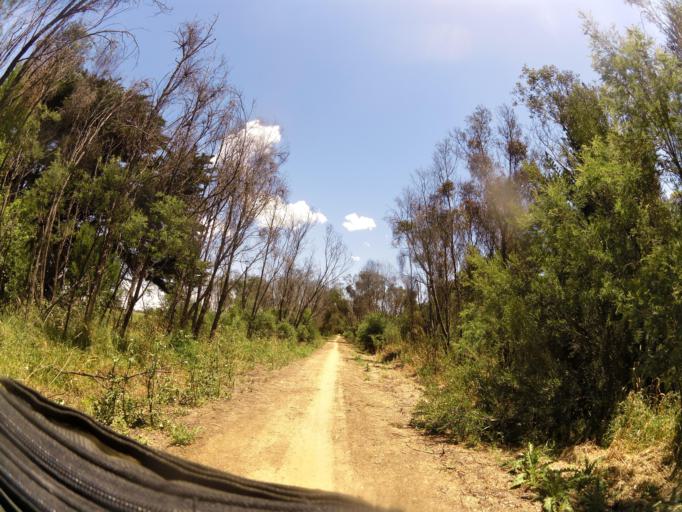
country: AU
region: Victoria
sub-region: Wellington
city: Heyfield
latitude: -37.9665
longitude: 146.9091
